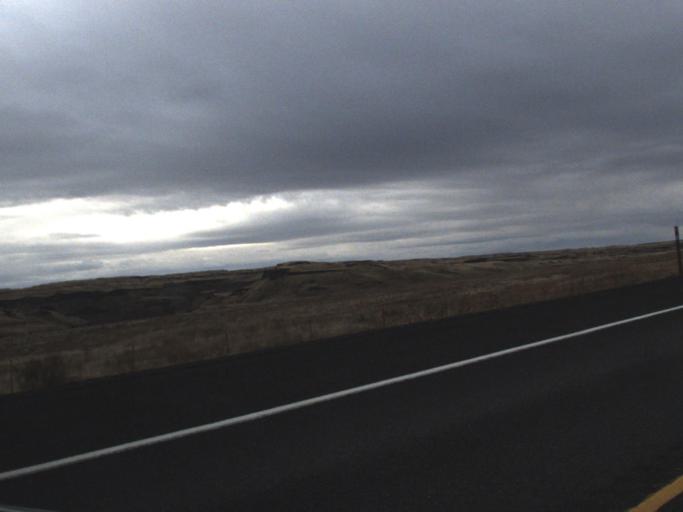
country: US
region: Washington
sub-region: Adams County
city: Ritzville
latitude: 46.7421
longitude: -118.2299
